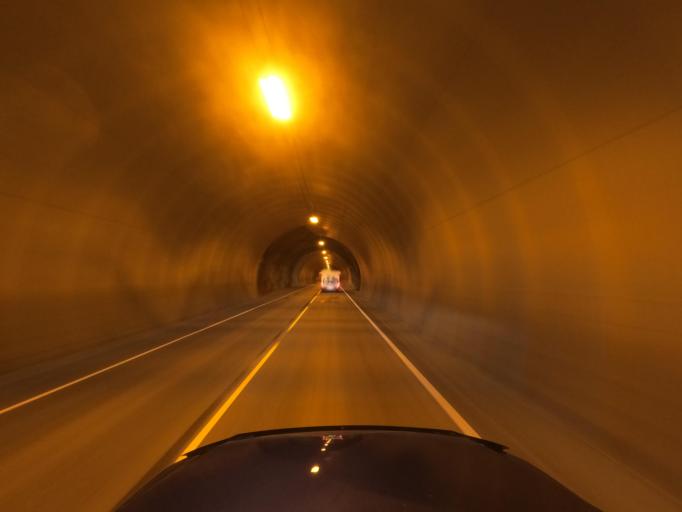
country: NO
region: Nordland
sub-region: Moskenes
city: Reine
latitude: 67.9248
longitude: 13.0811
